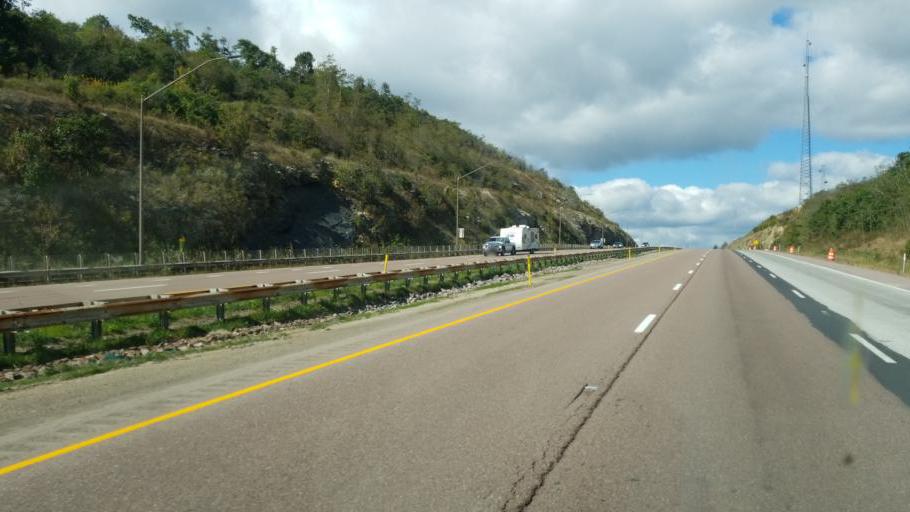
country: US
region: Maryland
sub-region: Allegany County
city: Frostburg
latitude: 39.6701
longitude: -78.9619
